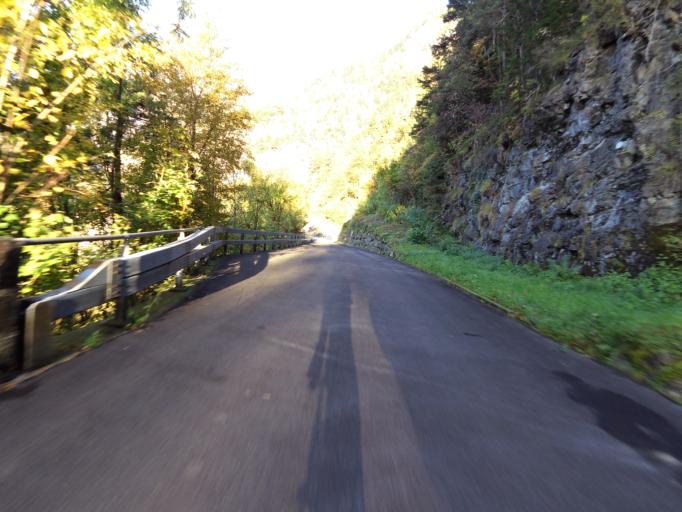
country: CH
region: Uri
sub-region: Uri
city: Bauen
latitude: 46.9417
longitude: 8.6180
